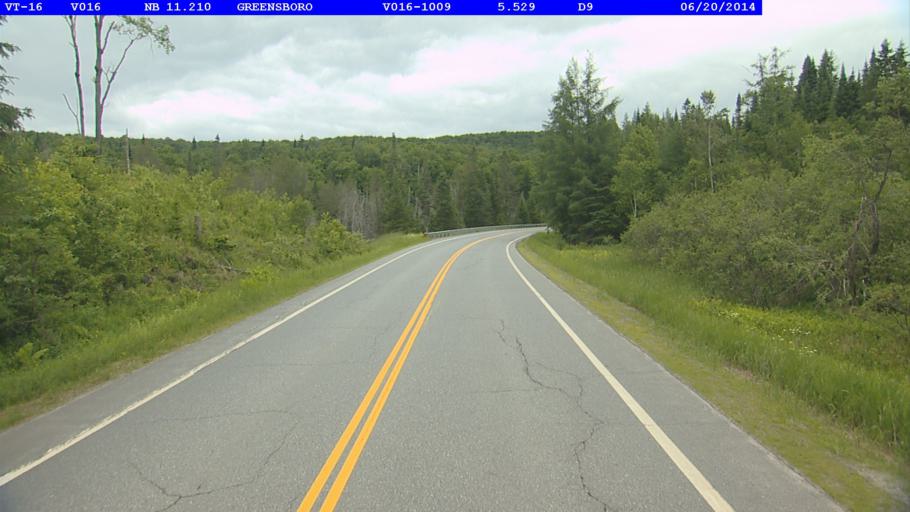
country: US
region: Vermont
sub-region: Caledonia County
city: Hardwick
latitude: 44.6243
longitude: -72.2126
